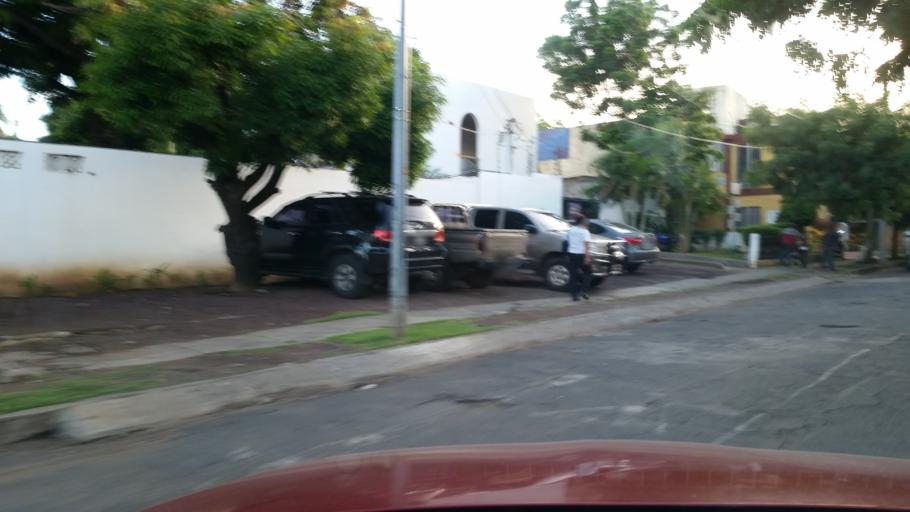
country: NI
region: Managua
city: Managua
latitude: 12.1401
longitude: -86.2855
